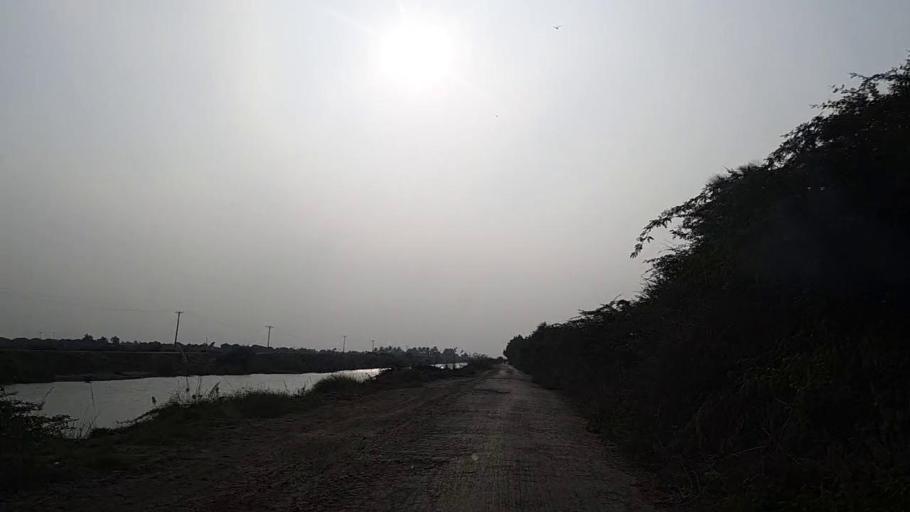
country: PK
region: Sindh
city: Mirpur Sakro
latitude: 24.6208
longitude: 67.5553
